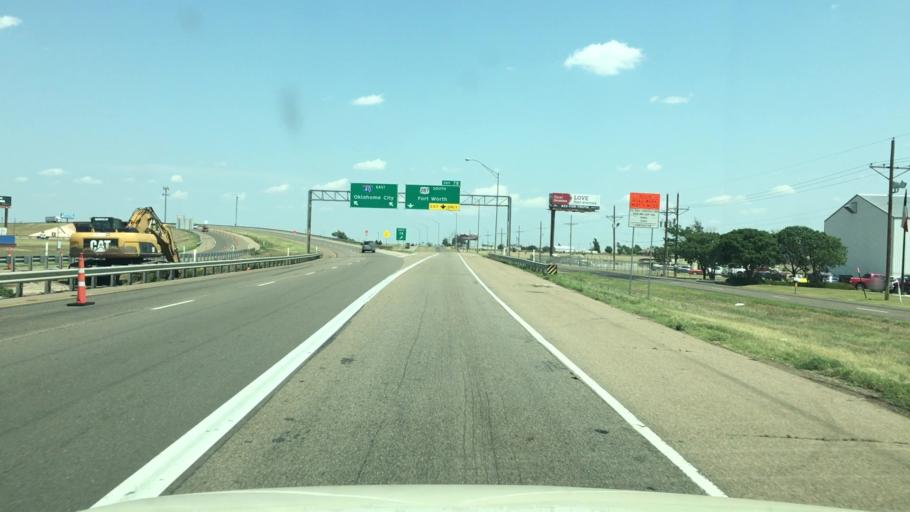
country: US
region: Texas
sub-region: Potter County
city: Amarillo
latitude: 35.1926
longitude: -101.6979
